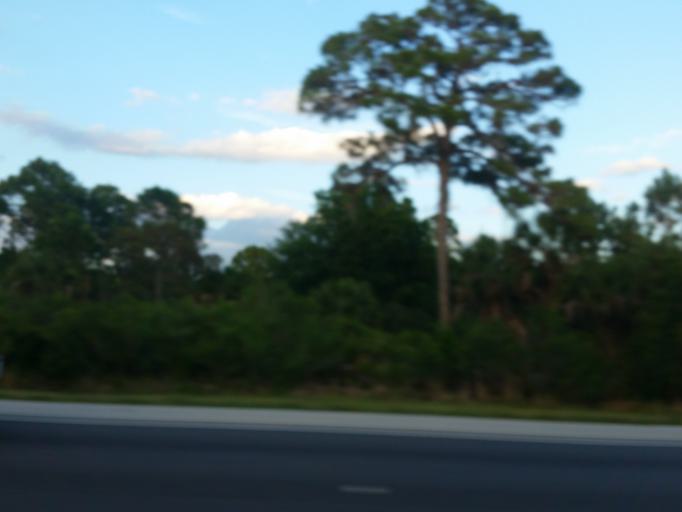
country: US
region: Florida
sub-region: Sarasota County
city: Vamo
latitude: 27.2291
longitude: -82.4515
